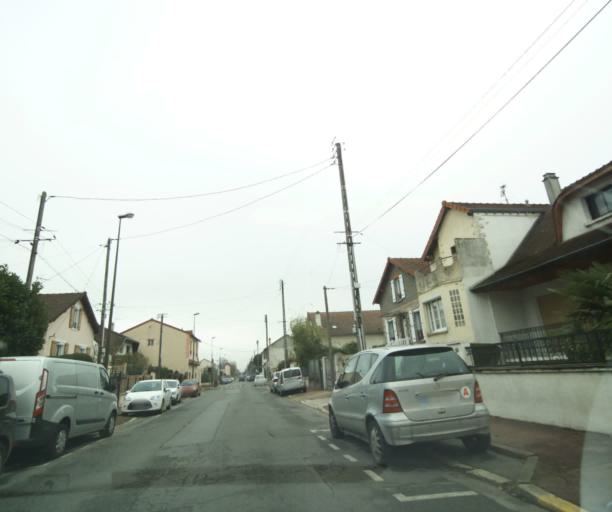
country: FR
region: Ile-de-France
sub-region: Departement de Seine-Saint-Denis
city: Le Raincy
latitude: 48.9161
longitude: 2.5215
